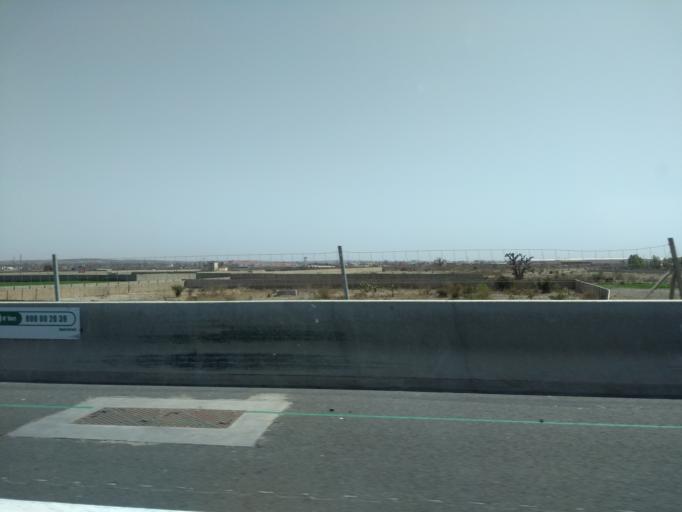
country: SN
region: Thies
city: Pout
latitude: 14.7351
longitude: -17.1661
